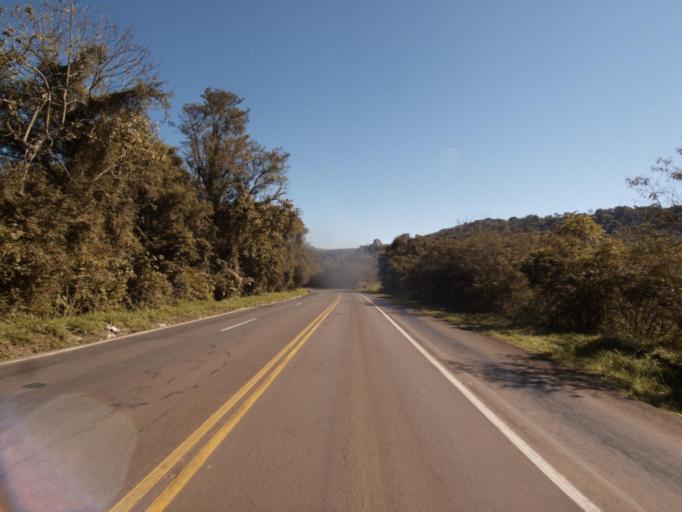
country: BR
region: Rio Grande do Sul
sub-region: Frederico Westphalen
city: Frederico Westphalen
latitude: -26.8190
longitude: -53.3710
